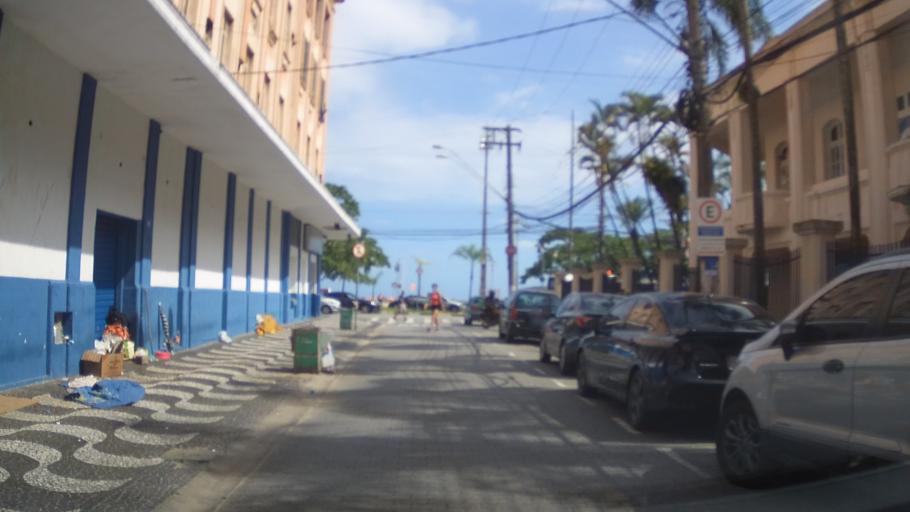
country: BR
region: Sao Paulo
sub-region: Santos
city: Santos
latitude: -23.9687
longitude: -46.3342
